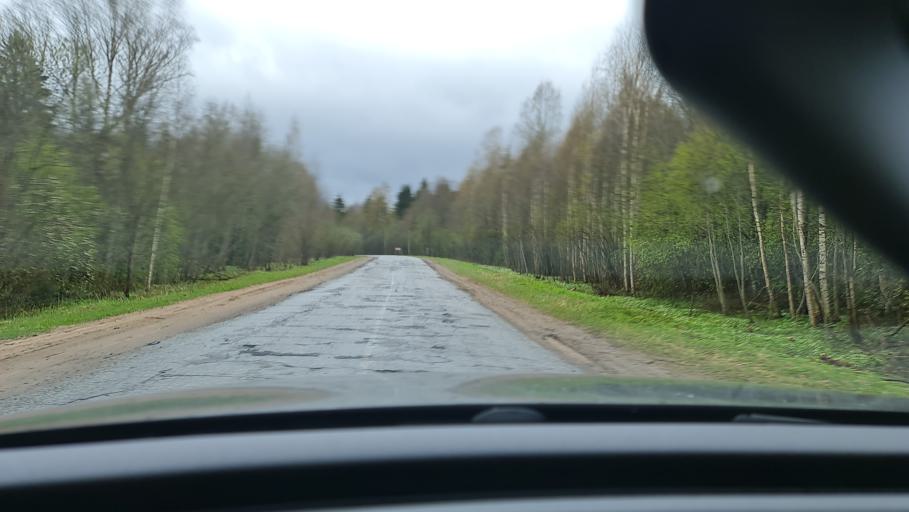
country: RU
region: Novgorod
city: Marevo
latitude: 57.2937
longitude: 32.0821
